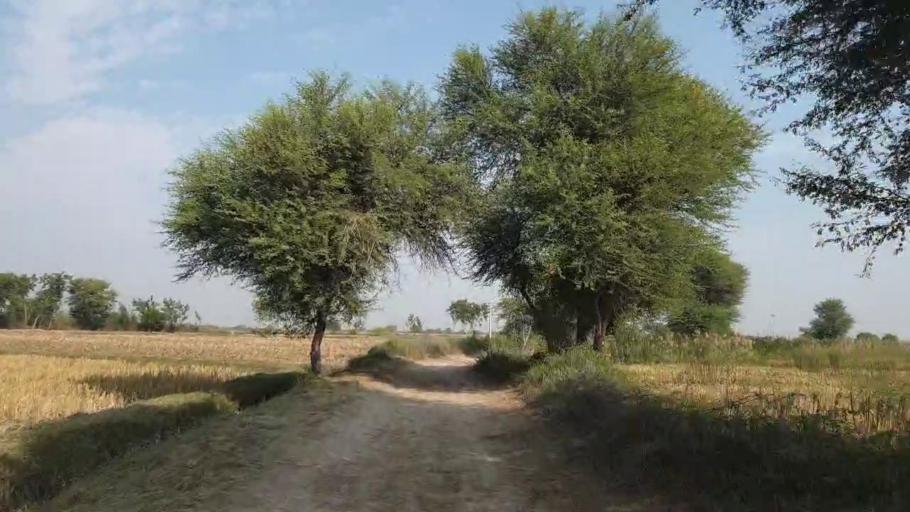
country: PK
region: Sindh
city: Tando Muhammad Khan
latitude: 25.0687
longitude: 68.4392
